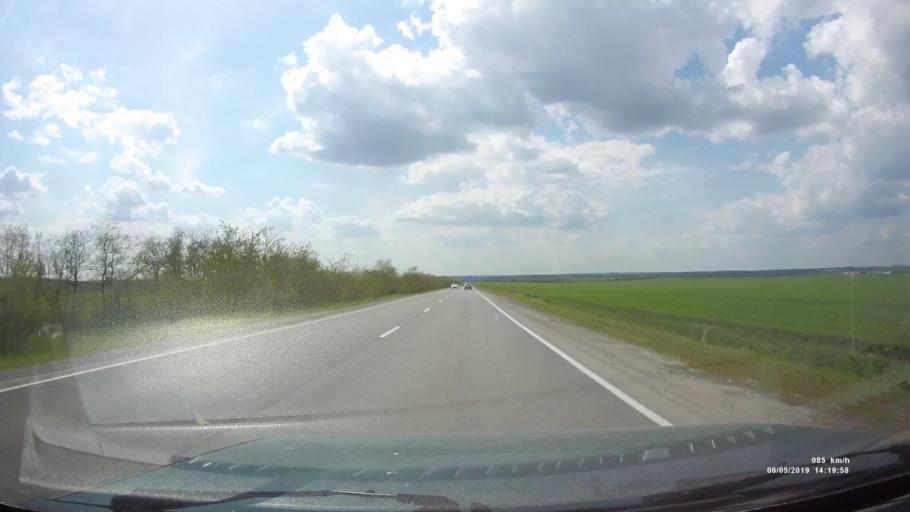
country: RU
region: Rostov
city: Kamenolomni
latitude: 47.6325
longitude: 40.2224
